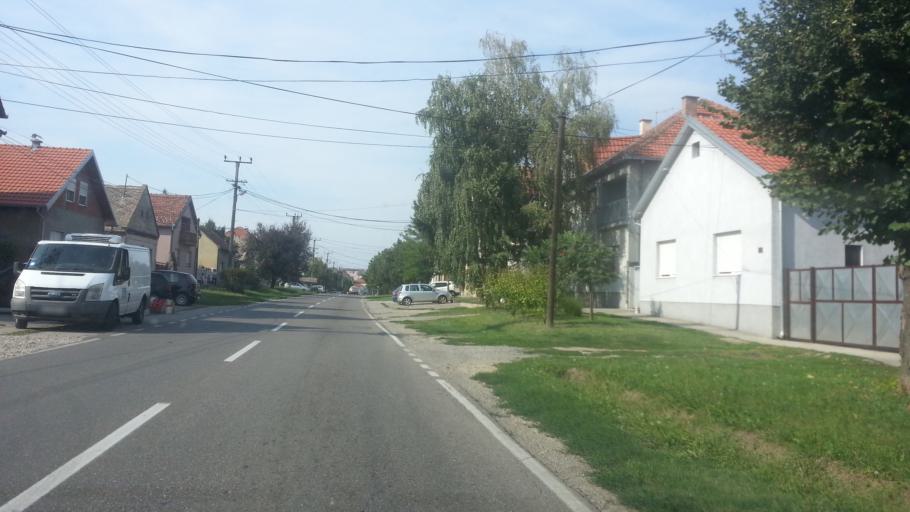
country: RS
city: Novi Banovci
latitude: 44.9524
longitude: 20.2819
